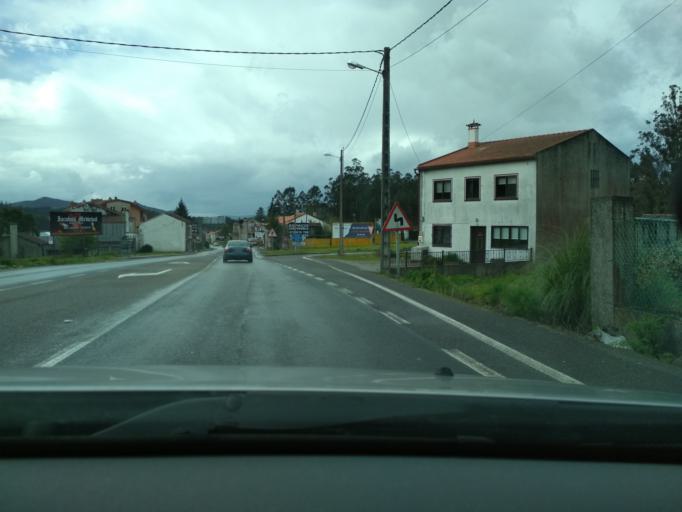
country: ES
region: Galicia
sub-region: Provincia da Coruna
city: Santiago de Compostela
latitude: 42.8356
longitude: -8.5877
